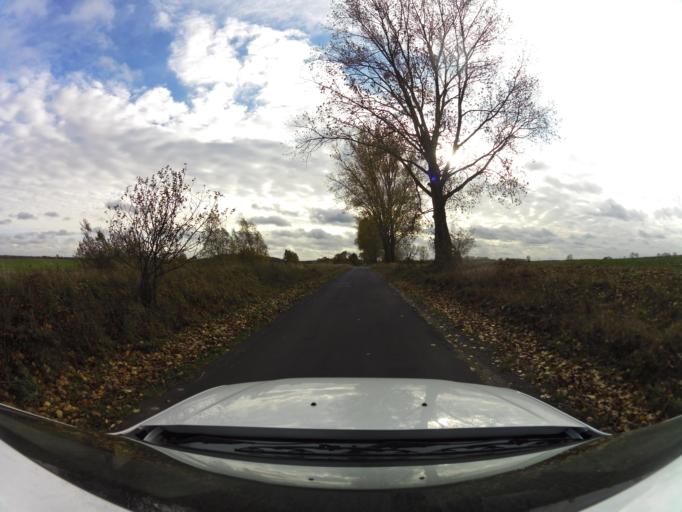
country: PL
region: West Pomeranian Voivodeship
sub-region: Powiat gryficki
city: Gryfice
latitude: 53.8977
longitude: 15.1287
